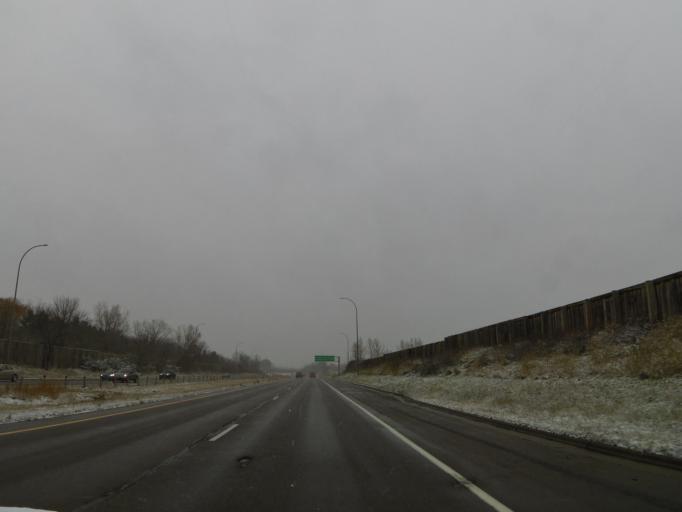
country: US
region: Minnesota
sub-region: Hennepin County
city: Edina
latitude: 44.8311
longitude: -93.3981
